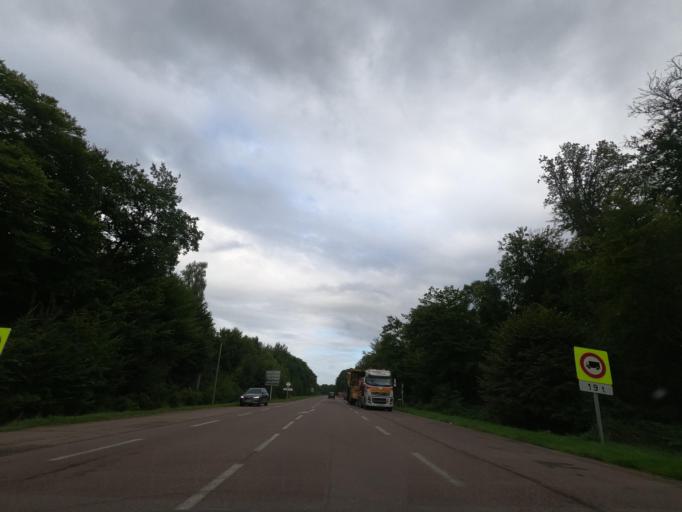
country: FR
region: Haute-Normandie
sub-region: Departement de la Seine-Maritime
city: Sahurs
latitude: 49.3432
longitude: 0.9359
